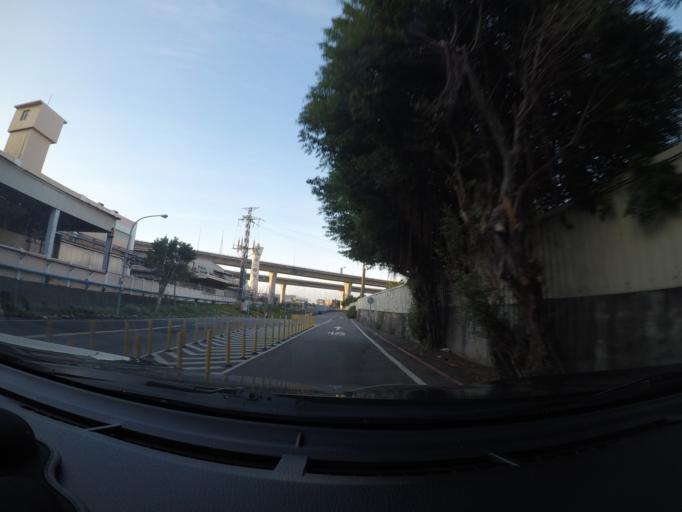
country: TW
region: Taiwan
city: Taoyuan City
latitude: 24.9941
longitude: 121.2454
